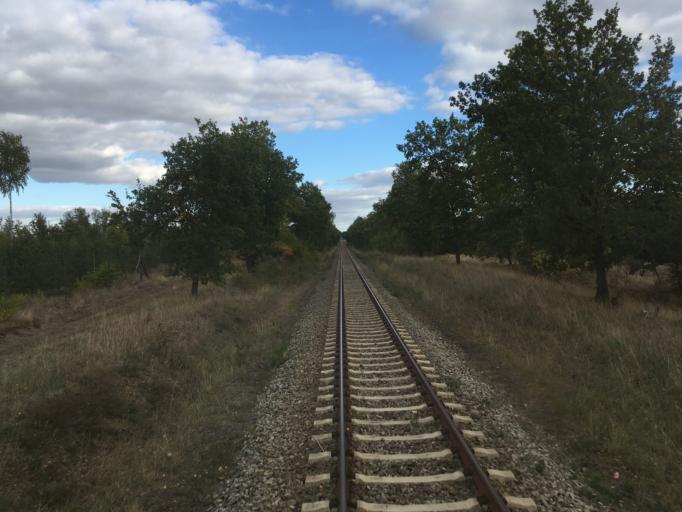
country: DE
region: Mecklenburg-Vorpommern
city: Grabowhofe
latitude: 53.5441
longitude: 12.5727
